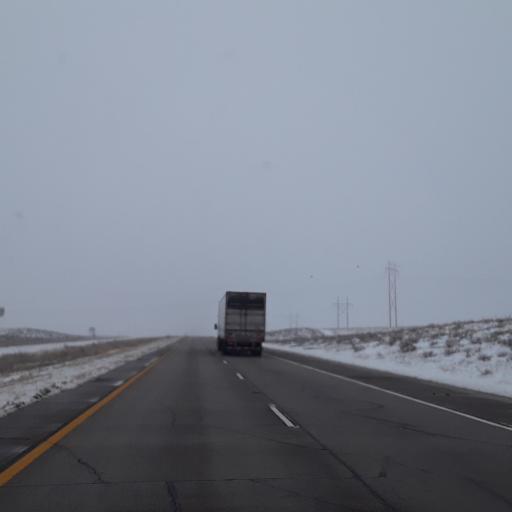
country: US
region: Colorado
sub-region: Logan County
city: Sterling
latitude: 40.7176
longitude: -103.0396
